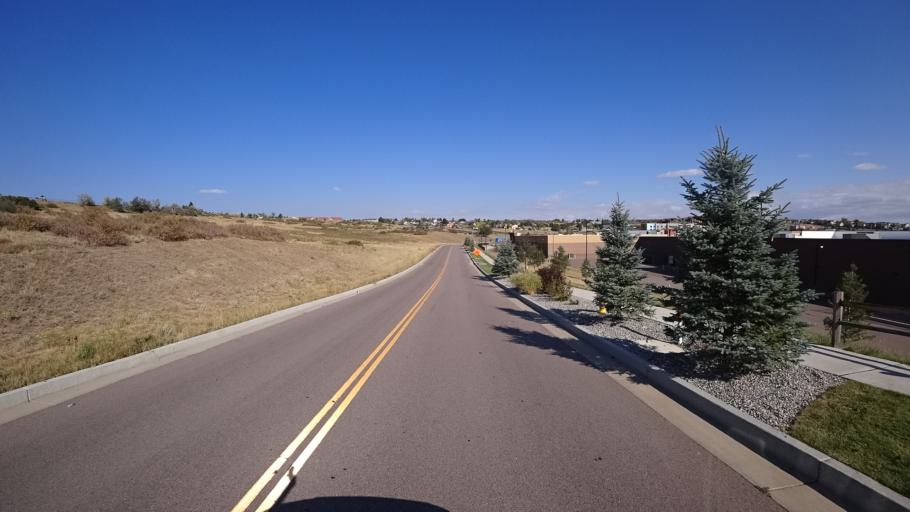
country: US
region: Colorado
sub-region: El Paso County
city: Cimarron Hills
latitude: 38.8916
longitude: -104.7230
